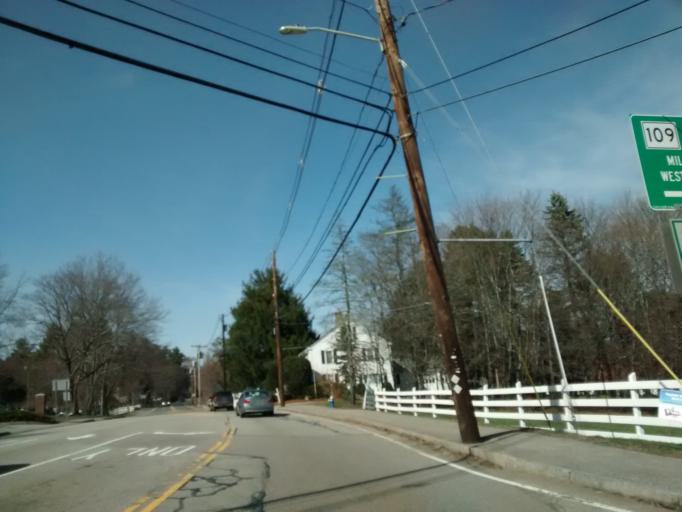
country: US
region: Massachusetts
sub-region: Norfolk County
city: Medway
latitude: 42.1523
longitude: -71.4084
